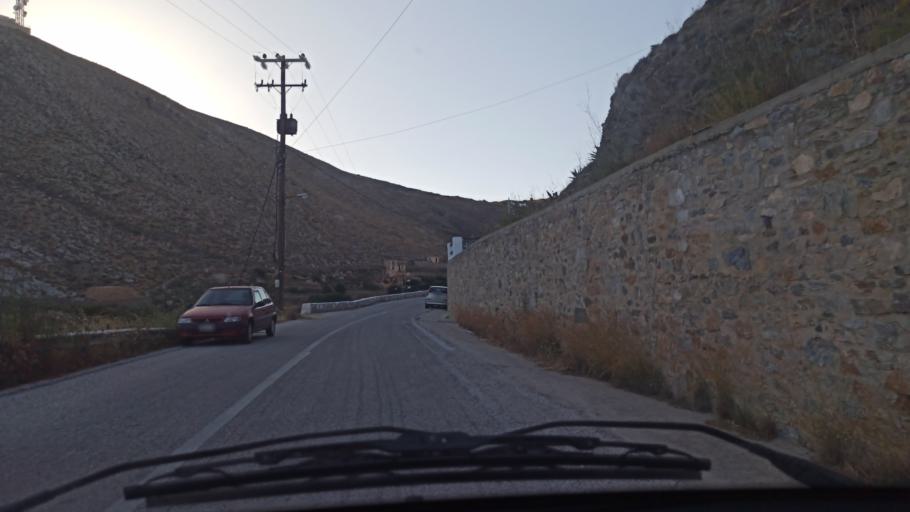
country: GR
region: South Aegean
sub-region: Nomos Kykladon
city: Ano Syros
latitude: 37.4564
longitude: 24.9323
